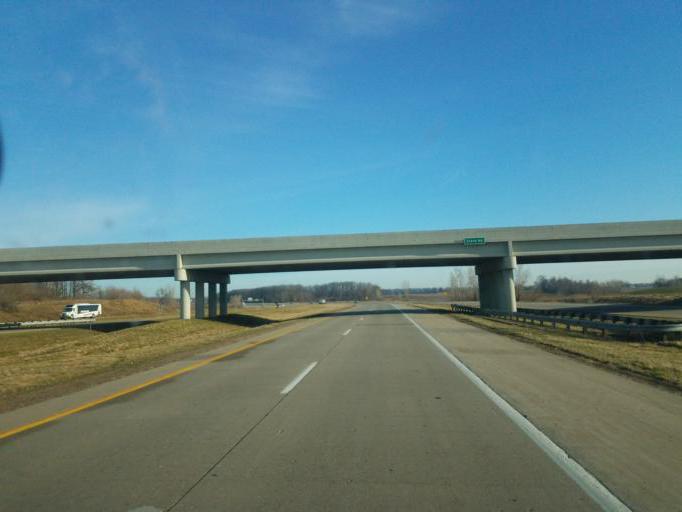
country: US
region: Michigan
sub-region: Clinton County
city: Bath
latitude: 42.8122
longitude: -84.5114
